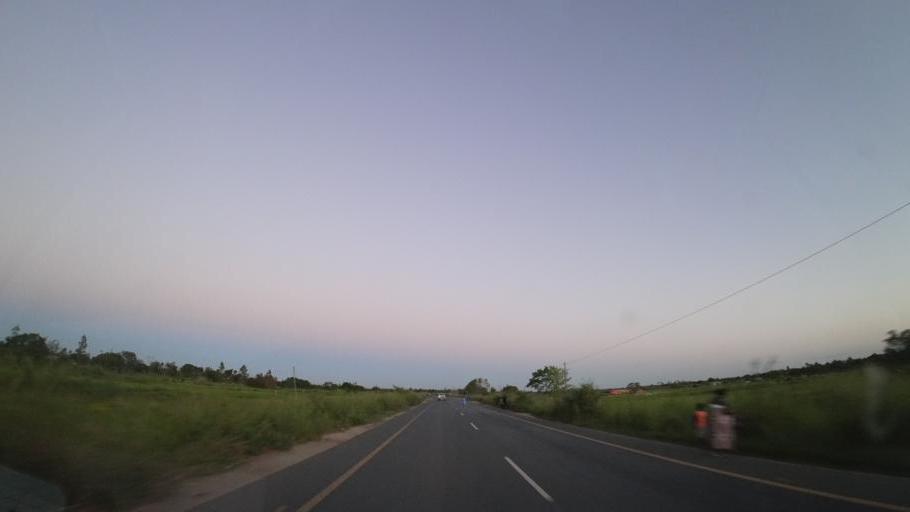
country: MZ
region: Sofala
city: Dondo
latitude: -19.5487
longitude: 34.6459
